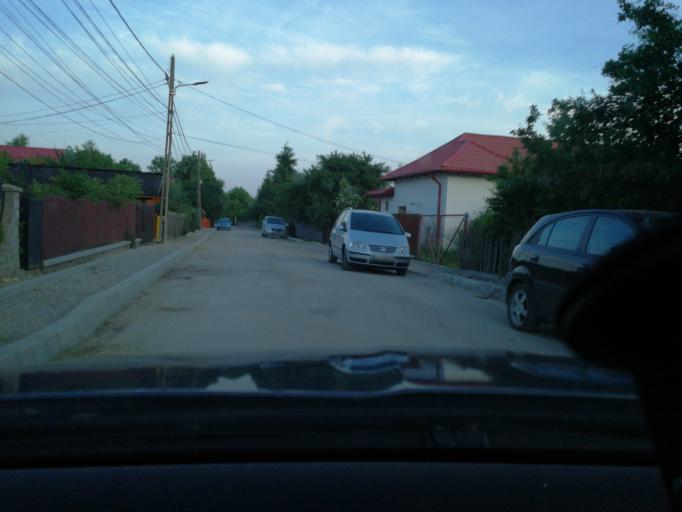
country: RO
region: Prahova
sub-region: Comuna Cornu
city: Cornu de Jos
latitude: 45.1591
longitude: 25.6979
